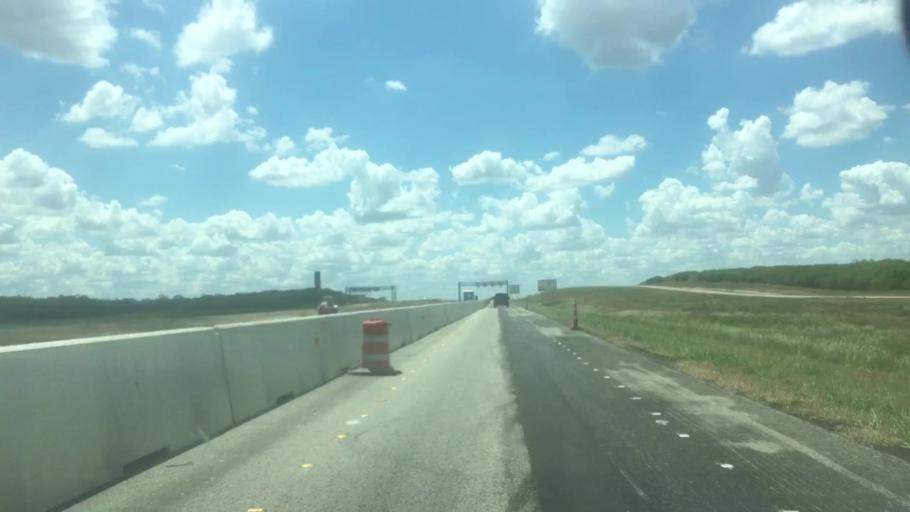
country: US
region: Texas
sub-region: Caldwell County
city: Martindale
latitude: 29.8174
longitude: -97.7589
